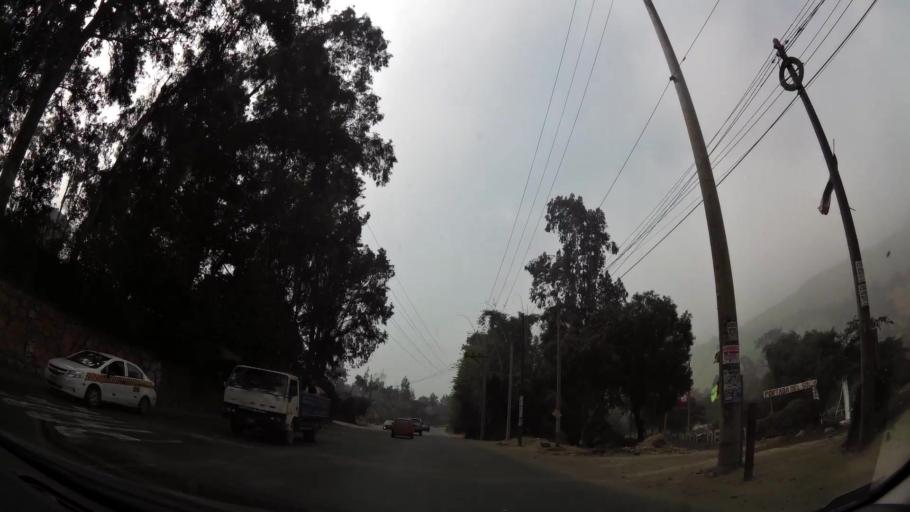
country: PE
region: Lima
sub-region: Lima
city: Chaclacayo
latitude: -11.9637
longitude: -76.7411
